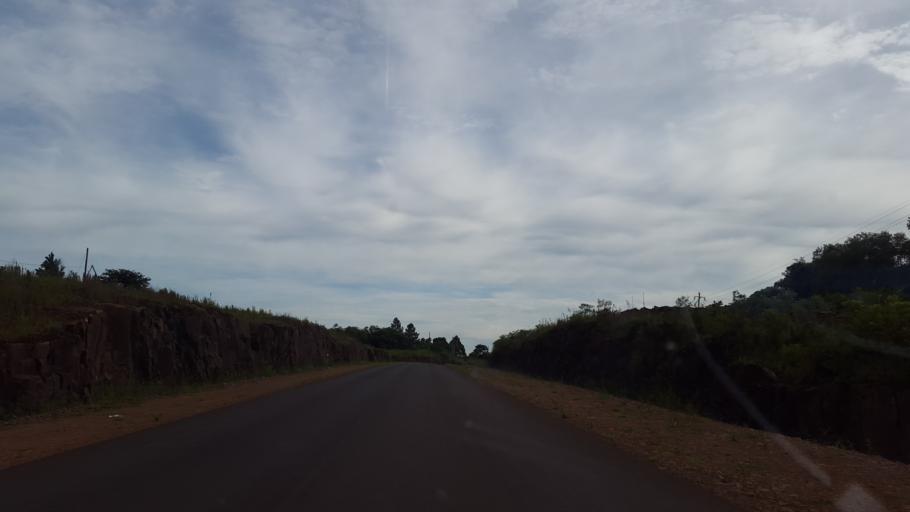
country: AR
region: Misiones
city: Bernardo de Irigoyen
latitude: -26.4319
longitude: -53.8525
